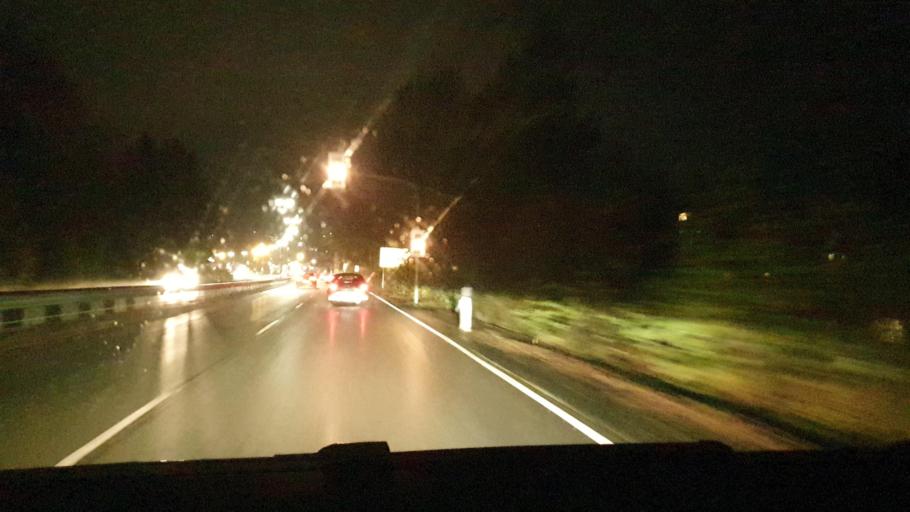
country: DE
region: North Rhine-Westphalia
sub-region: Regierungsbezirk Arnsberg
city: Siegen
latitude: 50.8863
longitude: 7.9604
